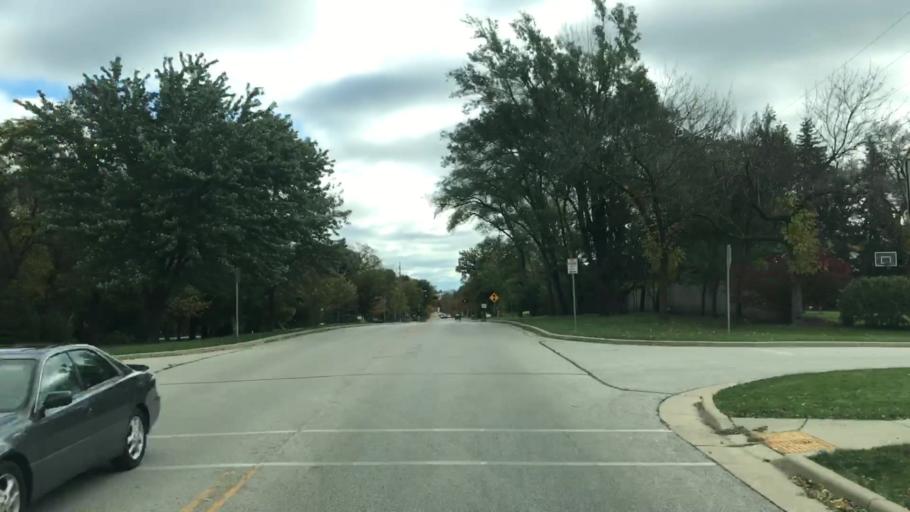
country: US
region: Wisconsin
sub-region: Waukesha County
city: Elm Grove
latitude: 43.0455
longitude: -88.0699
